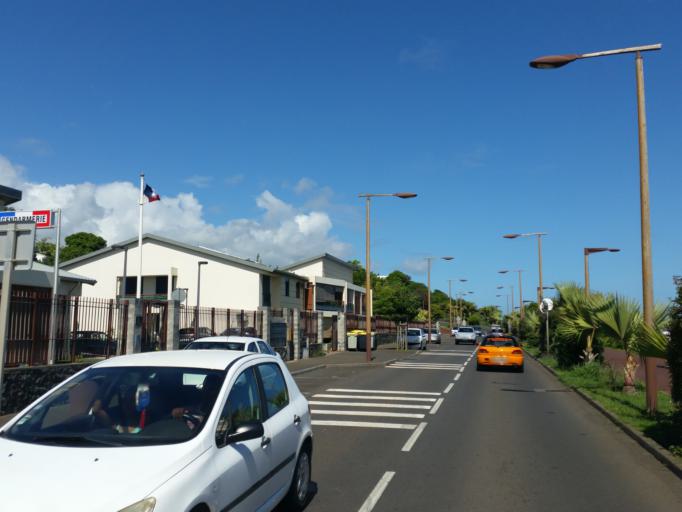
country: RE
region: Reunion
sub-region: Reunion
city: Sainte-Marie
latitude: -20.8956
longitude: 55.5463
